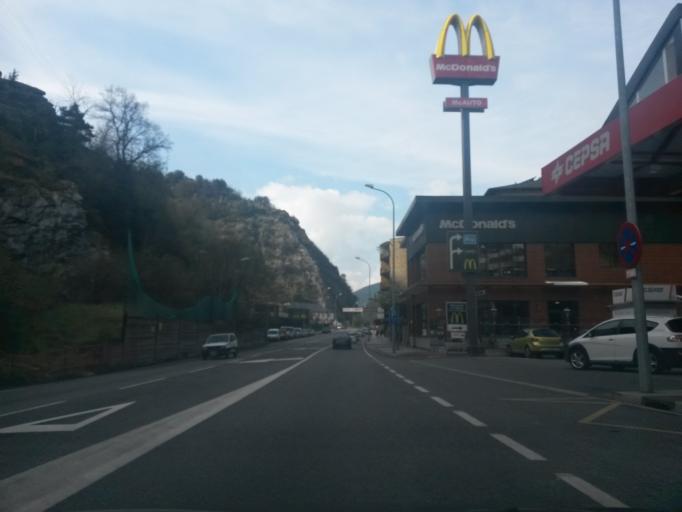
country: AD
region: Sant Julia de Loria
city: Sant Julia de Loria
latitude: 42.4602
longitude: 1.4893
